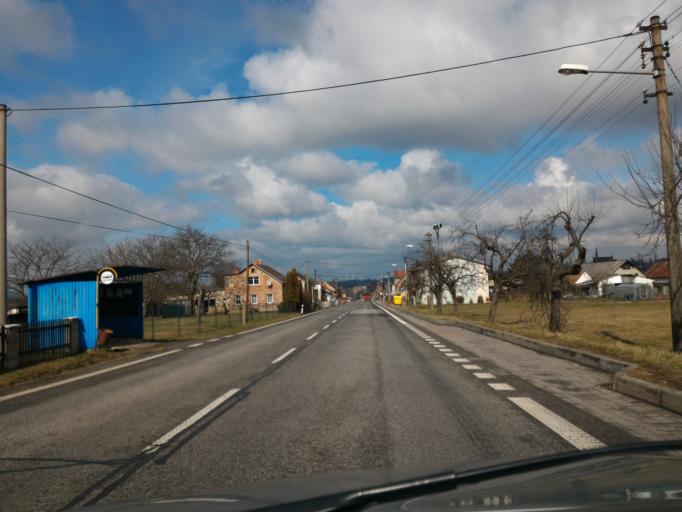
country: PL
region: Silesian Voivodeship
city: Zawidow
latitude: 51.0149
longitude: 15.0667
